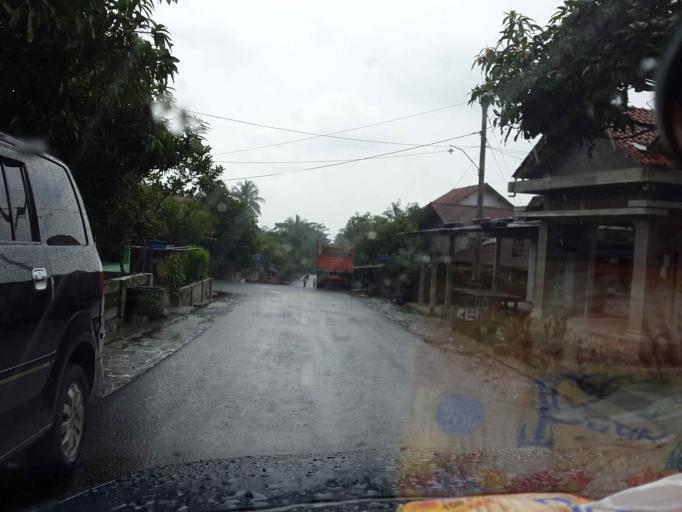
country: ID
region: Central Java
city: Muntilan
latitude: -7.5828
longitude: 110.3552
